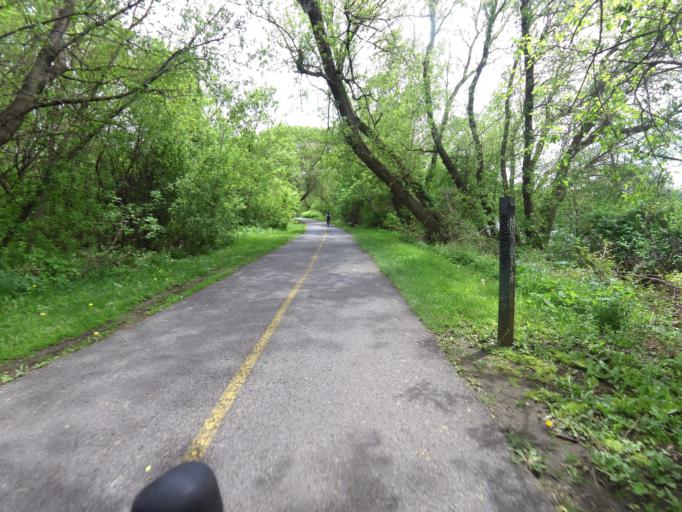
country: CA
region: Ontario
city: Ottawa
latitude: 45.4095
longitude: -75.6720
